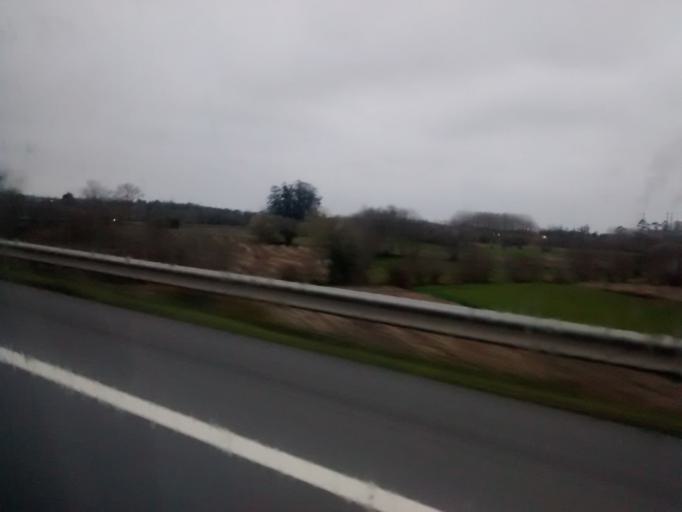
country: PT
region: Aveiro
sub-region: Aveiro
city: Eixo
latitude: 40.6803
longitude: -8.5691
